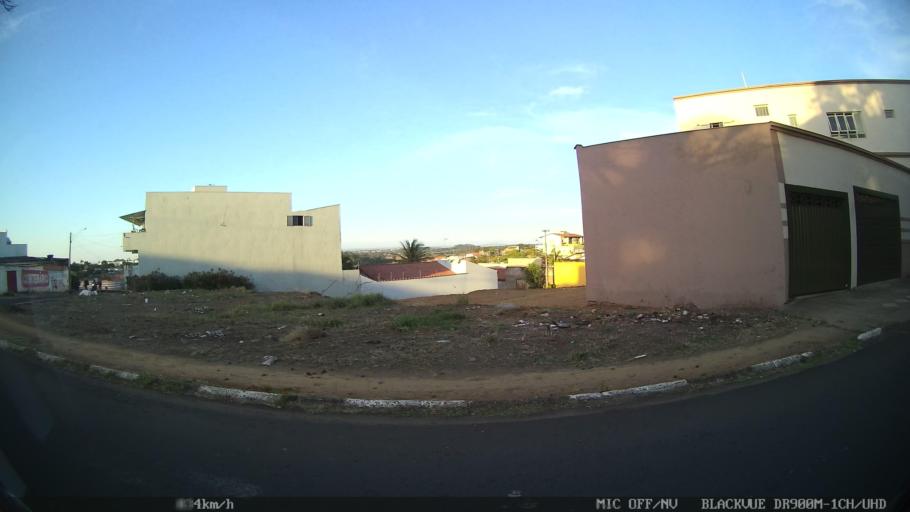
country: BR
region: Sao Paulo
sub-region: Franca
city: Franca
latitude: -20.5038
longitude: -47.3977
